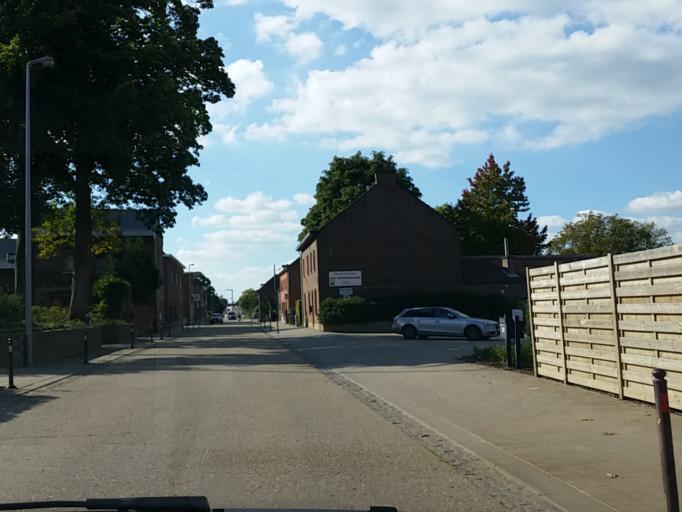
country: BE
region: Flanders
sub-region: Provincie Vlaams-Brabant
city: Holsbeek
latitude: 50.9206
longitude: 4.7662
